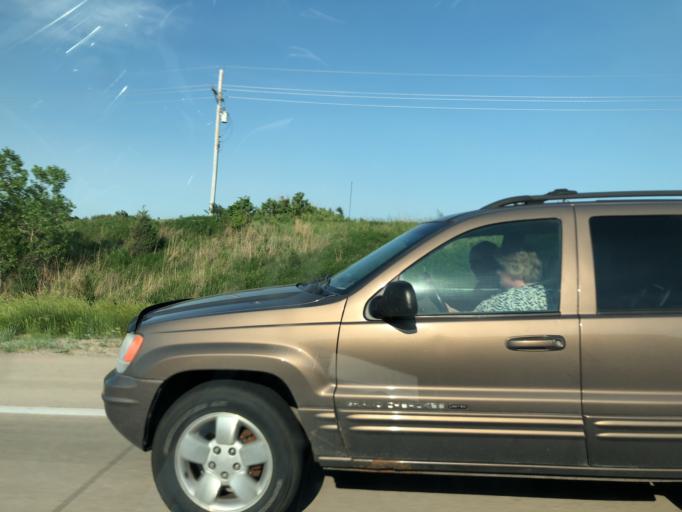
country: US
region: Nebraska
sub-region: Sarpy County
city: Gretna
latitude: 41.1022
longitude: -96.2534
